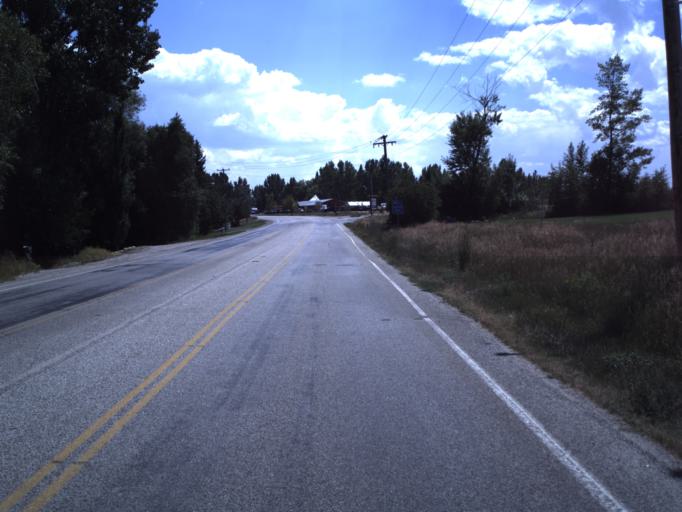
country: US
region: Idaho
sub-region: Bear Lake County
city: Paris
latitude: 41.9590
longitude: -111.4001
